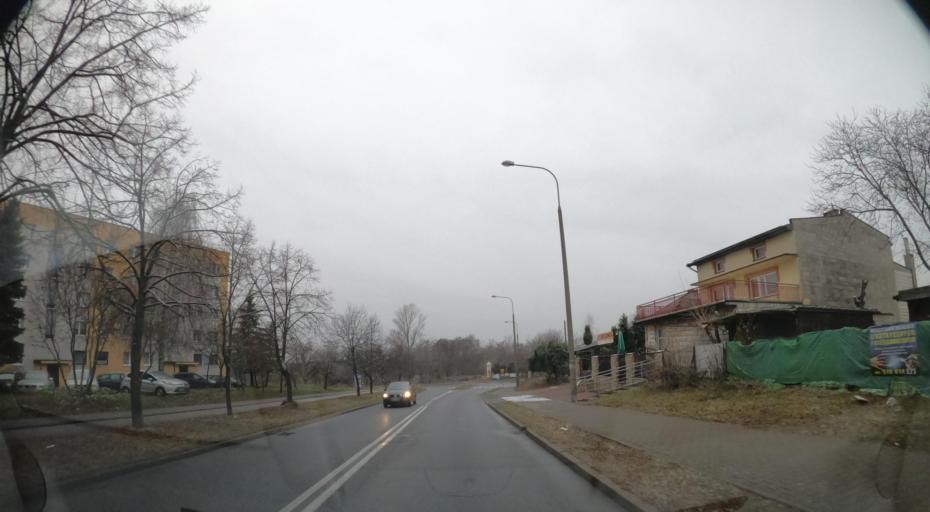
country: PL
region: Masovian Voivodeship
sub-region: Powiat radomski
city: Trablice
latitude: 51.3729
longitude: 21.1278
